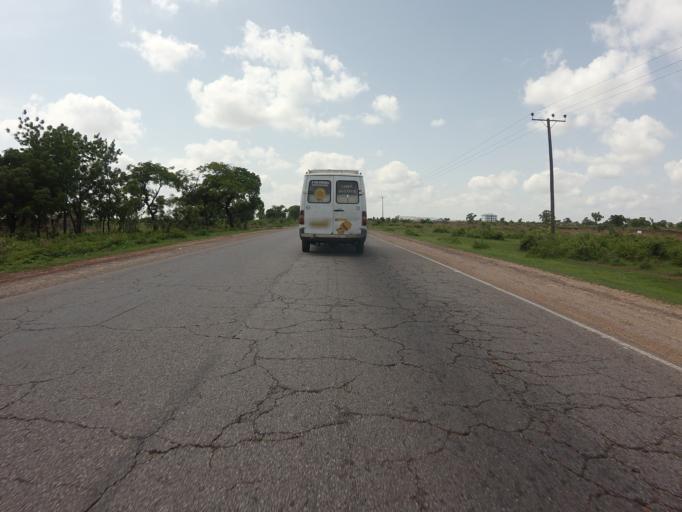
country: GH
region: Northern
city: Savelugu
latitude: 9.5819
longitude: -0.8336
